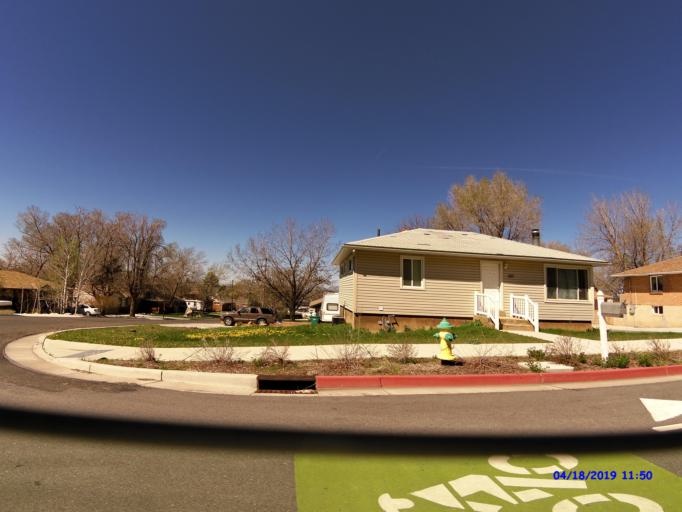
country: US
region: Utah
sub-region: Weber County
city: Harrisville
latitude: 41.2651
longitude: -111.9479
